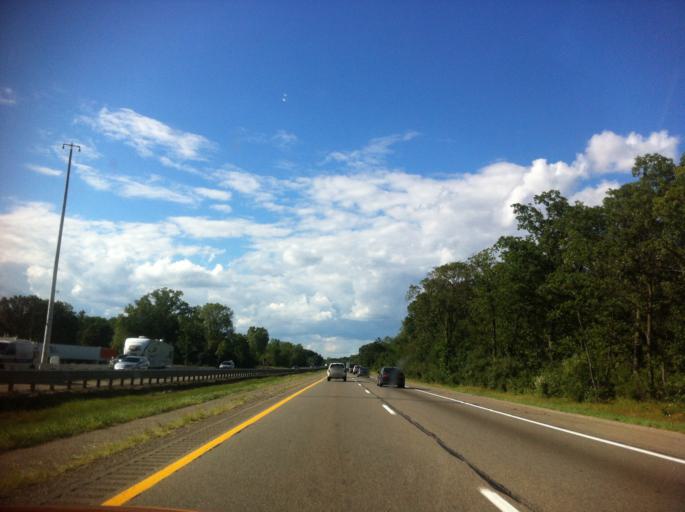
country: US
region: Michigan
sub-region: Washtenaw County
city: Ann Arbor
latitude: 42.3541
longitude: -83.7475
